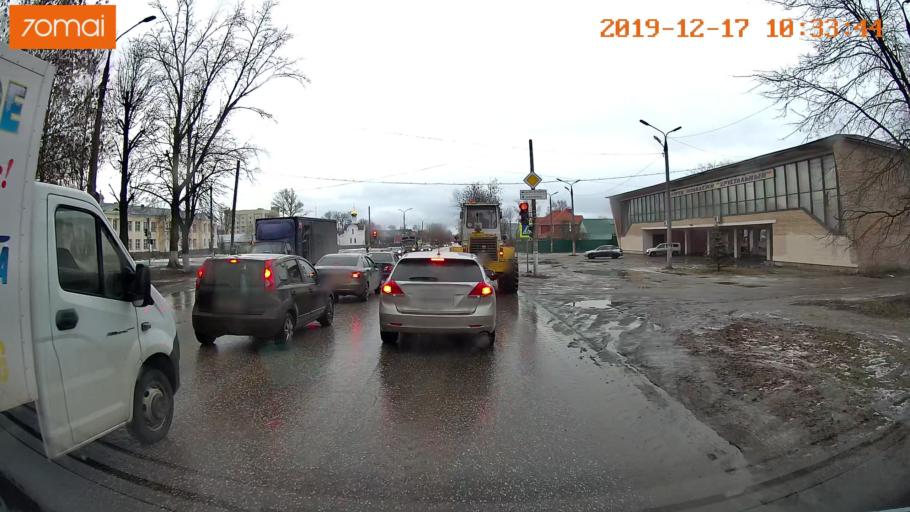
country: RU
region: Vladimir
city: Gus'-Khrustal'nyy
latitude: 55.6213
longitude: 40.6791
